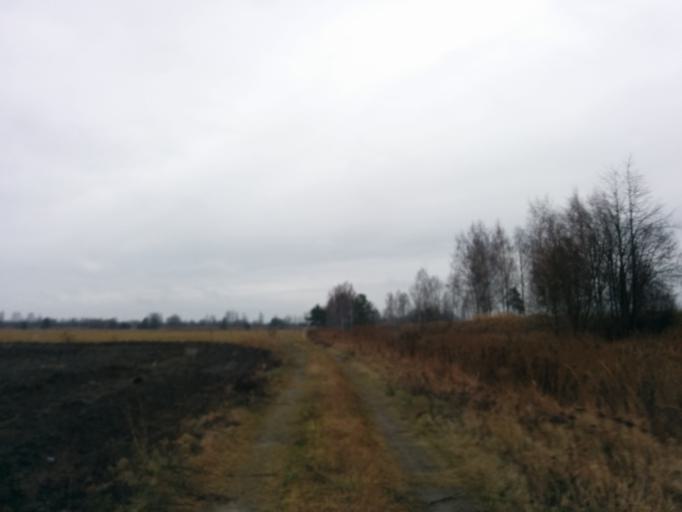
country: LV
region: Jelgava
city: Jelgava
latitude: 56.6801
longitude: 23.6677
